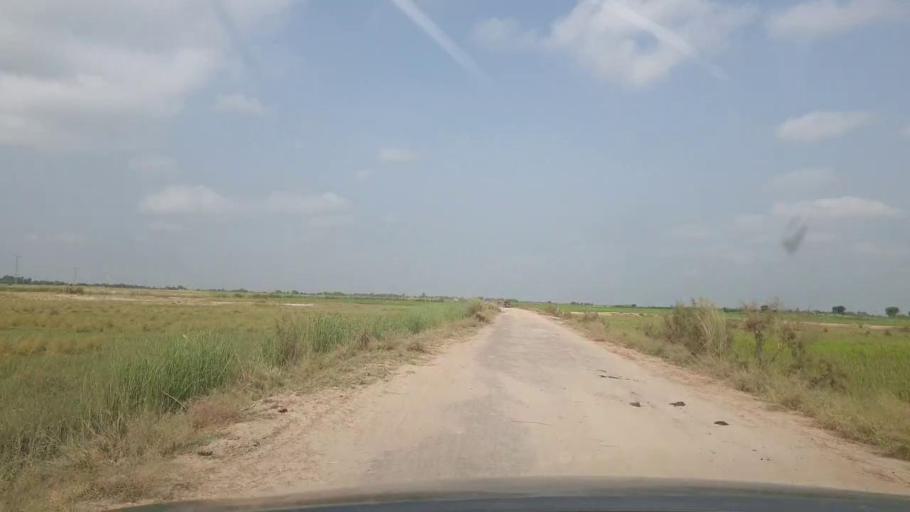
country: PK
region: Sindh
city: Ratodero
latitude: 27.8420
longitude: 68.2916
